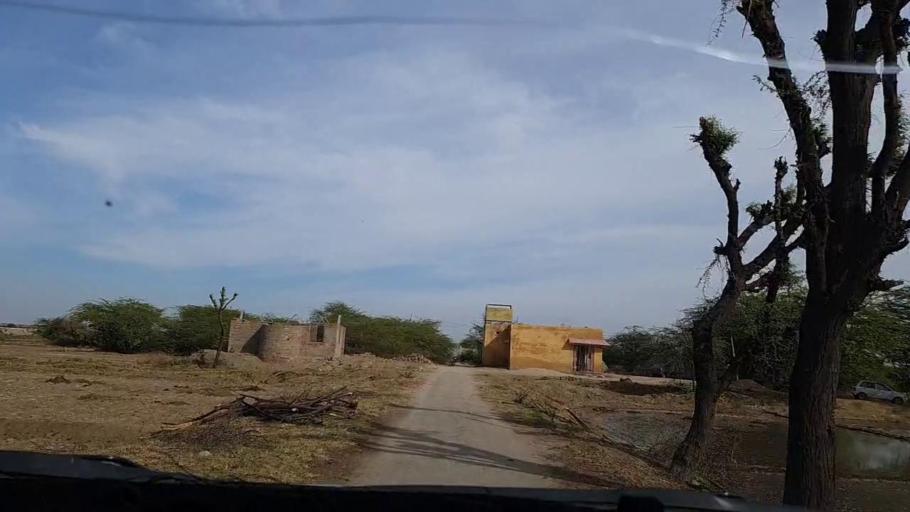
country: PK
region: Sindh
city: Dhoro Naro
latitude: 25.5026
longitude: 69.5335
